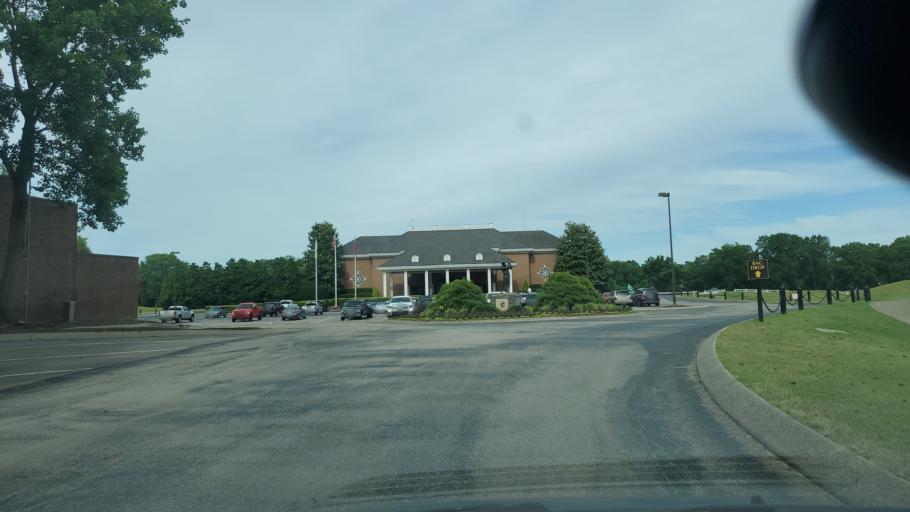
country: US
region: Tennessee
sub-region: Davidson County
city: Lakewood
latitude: 36.2201
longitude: -86.6819
